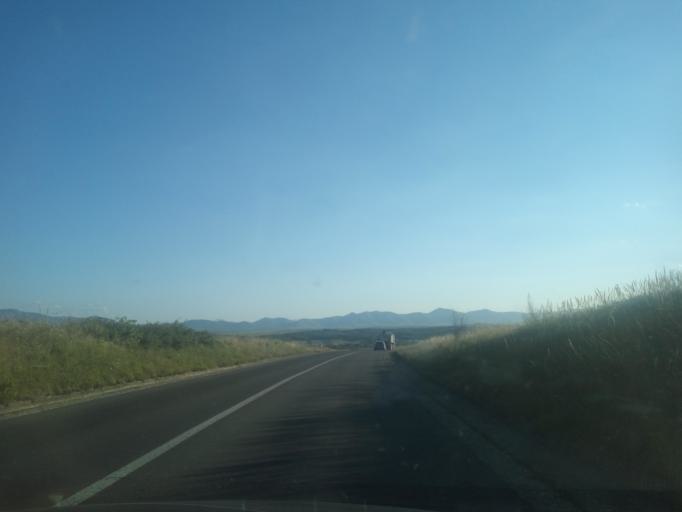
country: XK
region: Gjakova
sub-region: Komuna e Gjakoves
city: Gjakove
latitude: 42.4417
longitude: 20.4898
